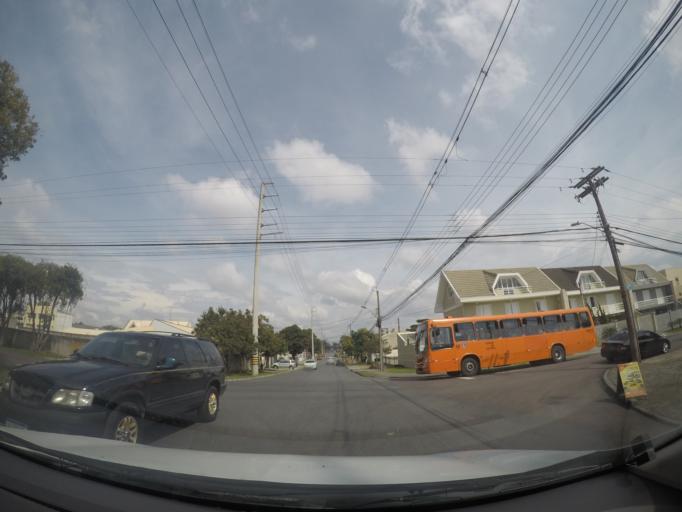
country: BR
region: Parana
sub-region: Curitiba
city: Curitiba
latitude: -25.4747
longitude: -49.2621
